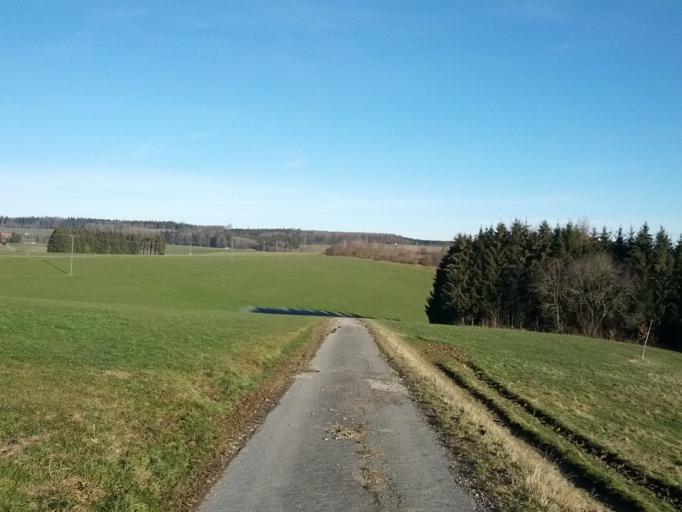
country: DE
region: Baden-Wuerttemberg
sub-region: Tuebingen Region
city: Steinhausen an der Rottum
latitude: 47.9859
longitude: 9.9875
